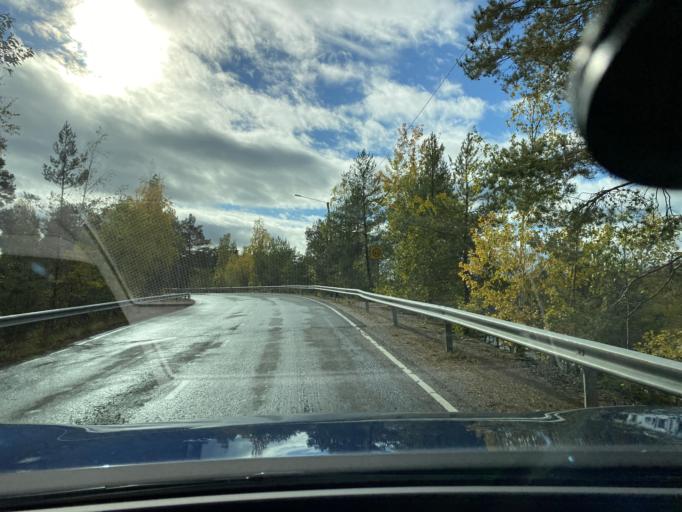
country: FI
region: Pirkanmaa
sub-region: Tampere
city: Nokia
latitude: 61.4788
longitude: 23.3400
